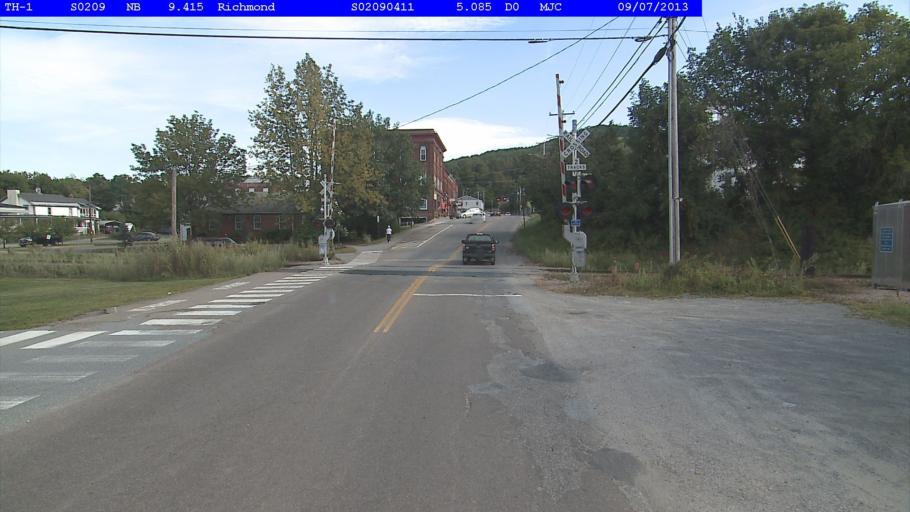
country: US
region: Vermont
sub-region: Chittenden County
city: Williston
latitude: 44.4039
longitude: -72.9944
